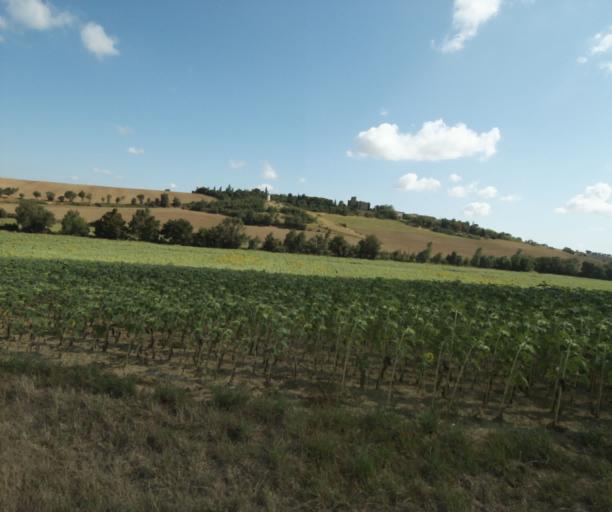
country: FR
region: Midi-Pyrenees
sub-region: Departement de la Haute-Garonne
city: Avignonet-Lauragais
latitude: 43.4457
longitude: 1.7850
